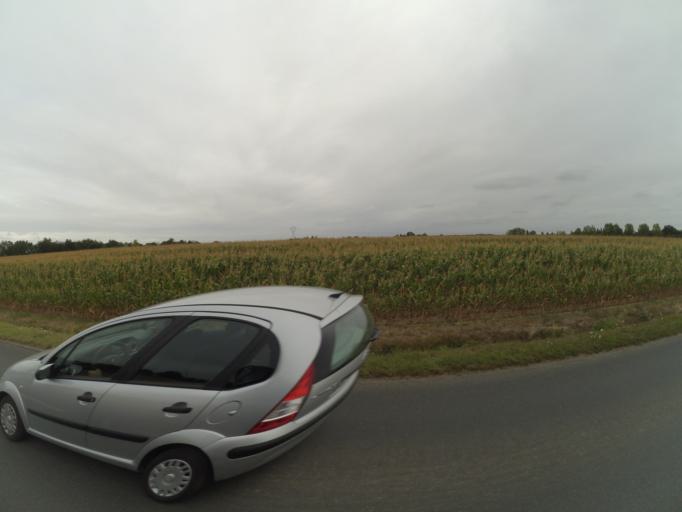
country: FR
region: Pays de la Loire
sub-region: Departement de la Vendee
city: Saint-Andre-Treize-Voies
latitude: 46.9246
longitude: -1.3973
